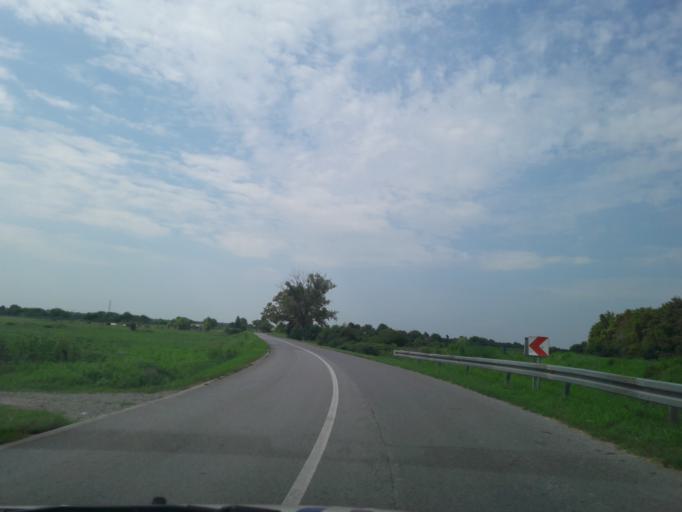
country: HR
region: Osjecko-Baranjska
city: Bizovac
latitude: 45.5059
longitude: 18.4523
